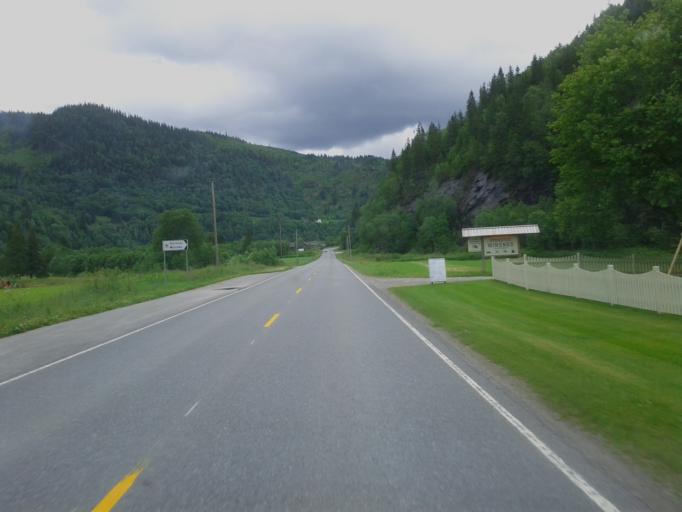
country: NO
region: Sor-Trondelag
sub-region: Midtre Gauldal
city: Storen
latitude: 62.9501
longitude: 10.6155
